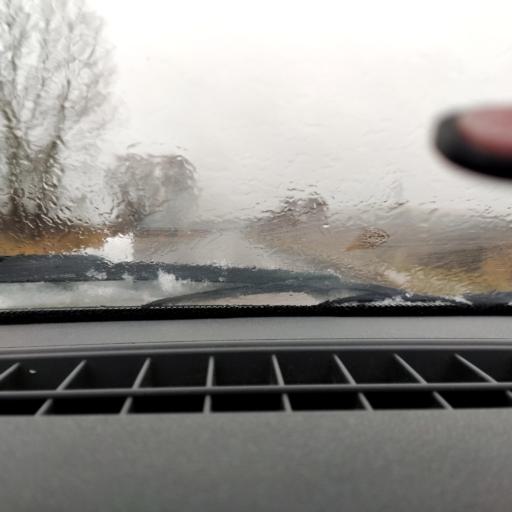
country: RU
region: Bashkortostan
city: Ufa
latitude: 54.8300
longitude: 56.1687
